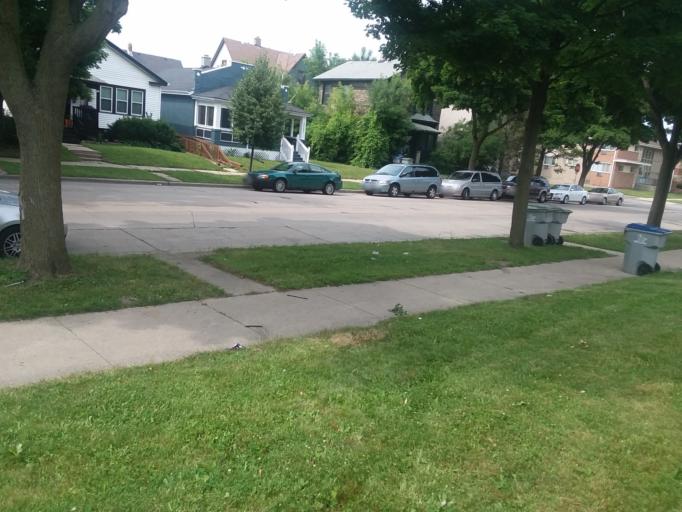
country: US
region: Wisconsin
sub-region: Milwaukee County
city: West Milwaukee
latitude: 43.0376
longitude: -87.9455
